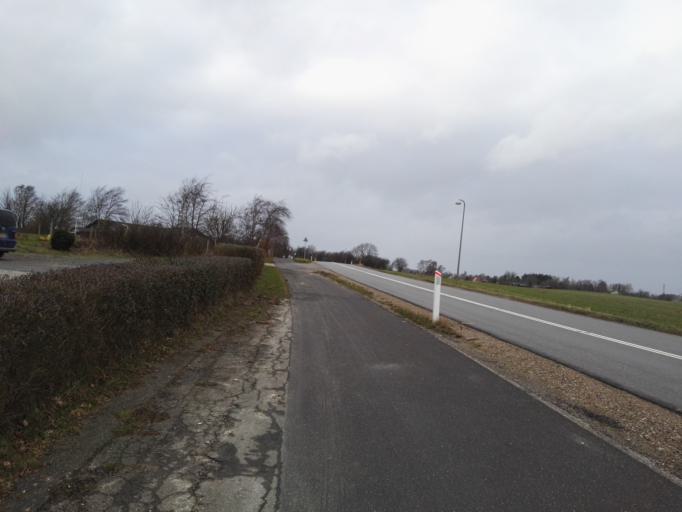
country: DK
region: Zealand
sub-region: Lejre Kommune
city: Ejby
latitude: 55.6974
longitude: 11.9076
